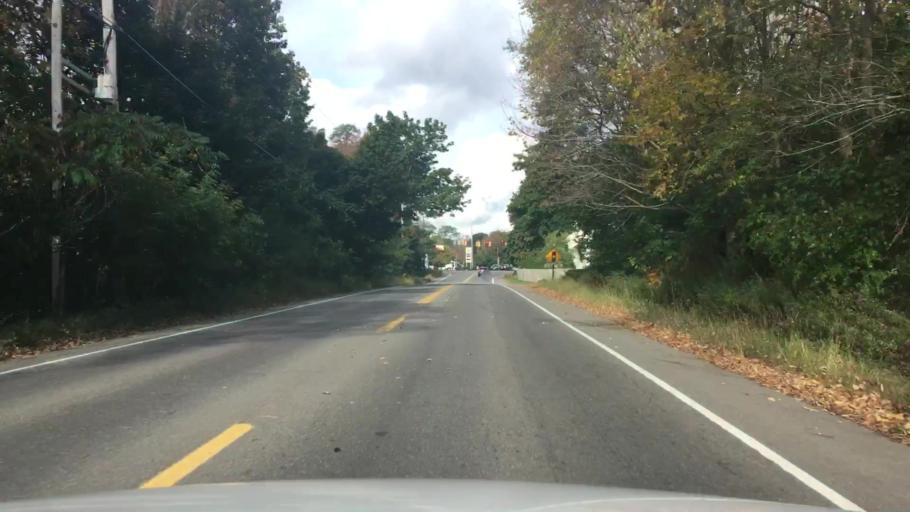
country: US
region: Maine
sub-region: Knox County
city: Rockland
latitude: 44.1224
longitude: -69.1157
